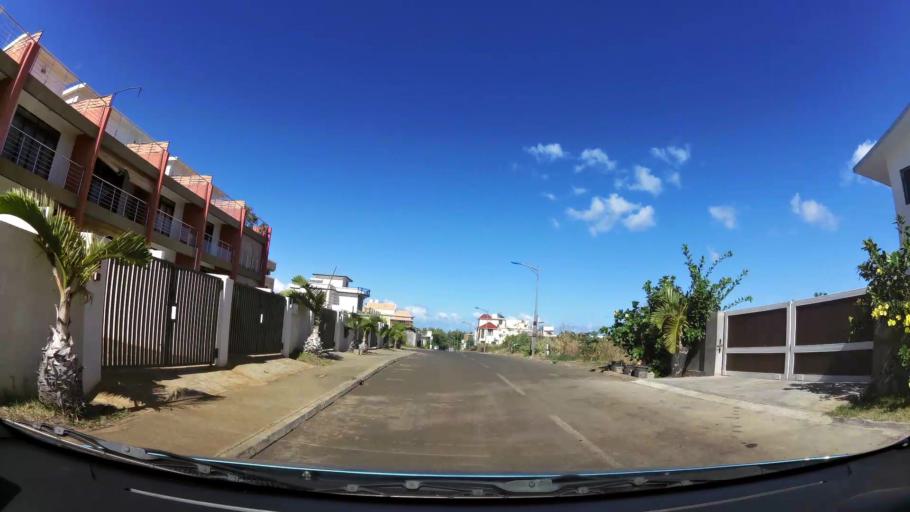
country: MU
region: Black River
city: Flic en Flac
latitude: -20.2831
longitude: 57.3749
